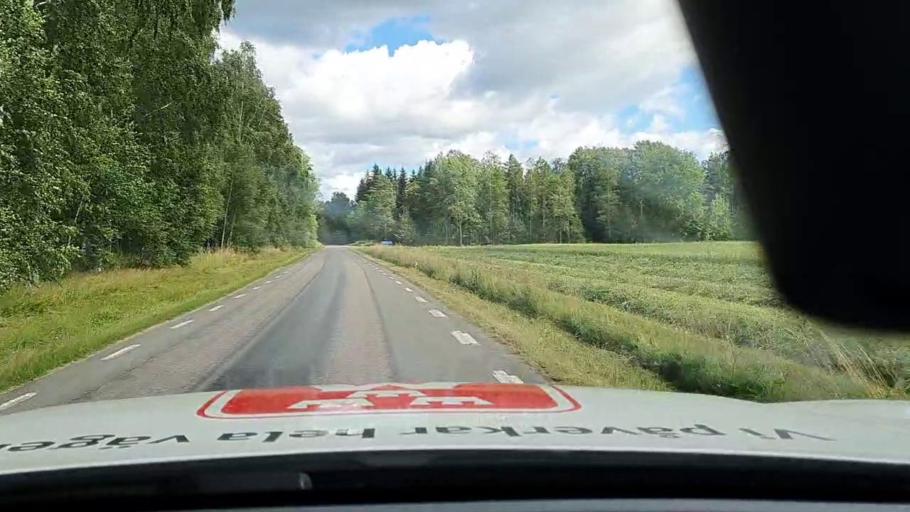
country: SE
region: Vaestra Goetaland
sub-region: Karlsborgs Kommun
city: Molltorp
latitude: 58.6100
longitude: 14.3459
